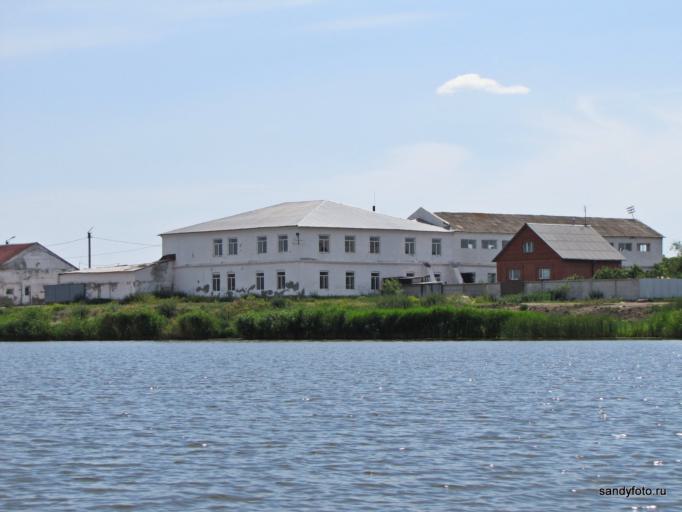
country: RU
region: Chelyabinsk
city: Troitsk
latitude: 54.0890
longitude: 61.5830
